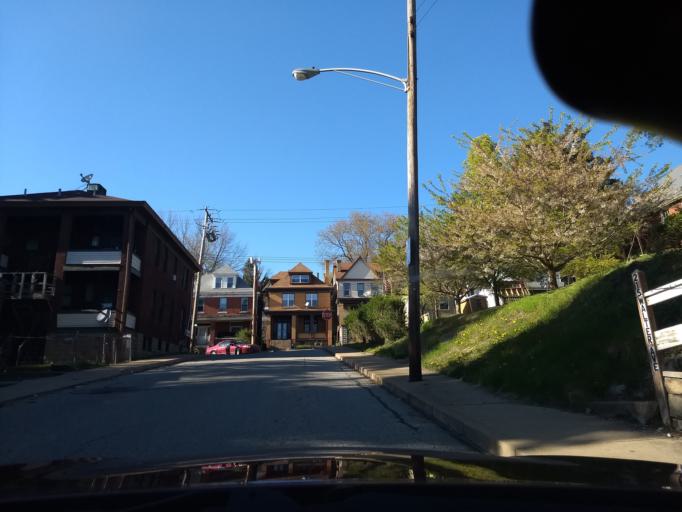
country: US
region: Pennsylvania
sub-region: Allegheny County
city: Mount Oliver
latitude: 40.4122
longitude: -79.9842
